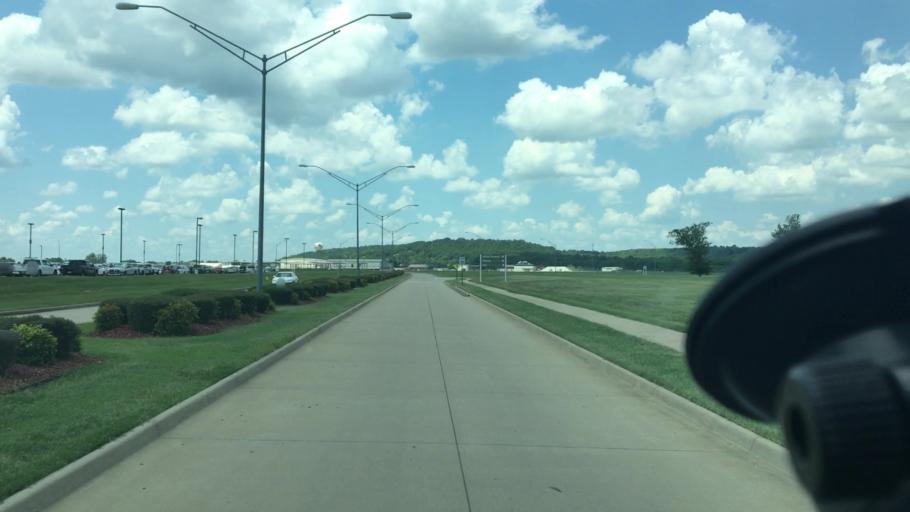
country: US
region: Arkansas
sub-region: Sebastian County
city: Barling
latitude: 35.3427
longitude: -94.3572
